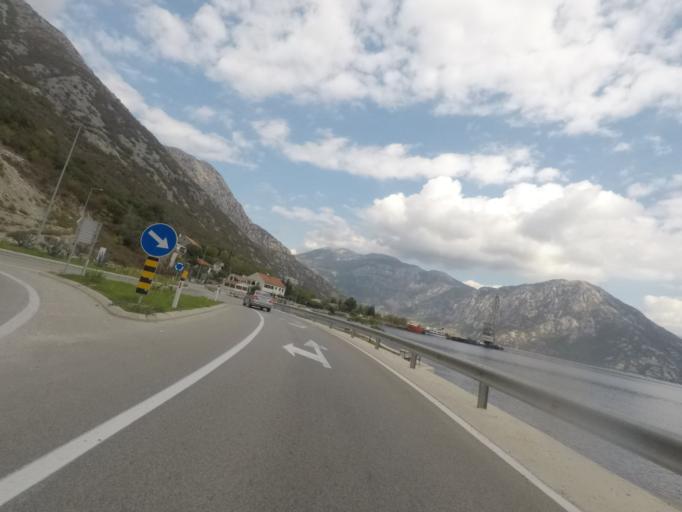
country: ME
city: Lipci
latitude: 42.4953
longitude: 18.6545
